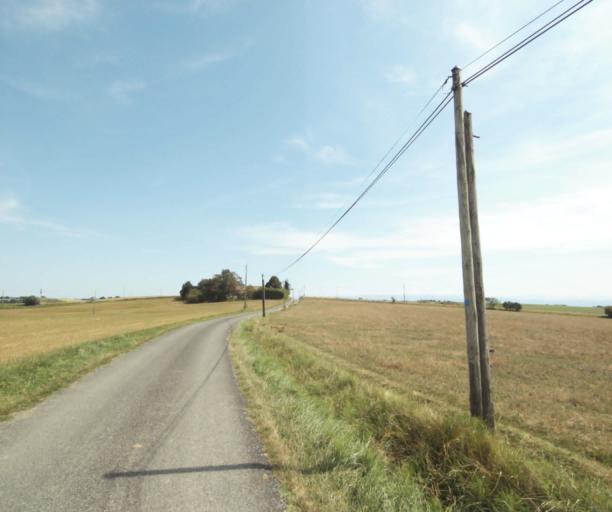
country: FR
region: Midi-Pyrenees
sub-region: Departement de la Haute-Garonne
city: Gaillac-Toulza
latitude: 43.2588
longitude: 1.4201
